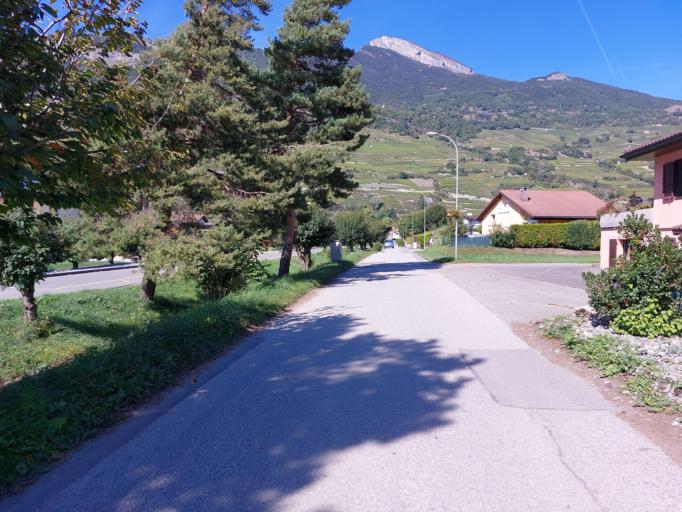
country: CH
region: Valais
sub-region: Conthey District
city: Vetroz
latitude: 46.2218
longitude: 7.2798
